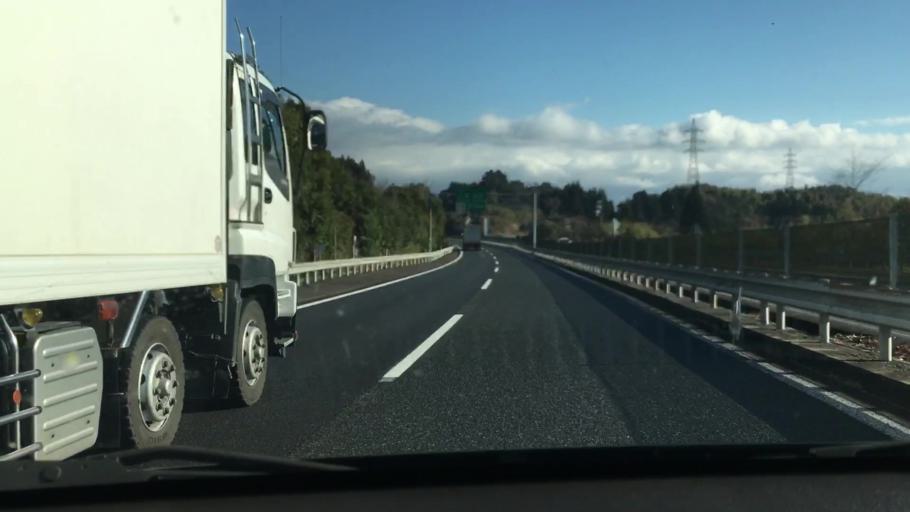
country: JP
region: Kumamoto
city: Hitoyoshi
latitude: 32.2361
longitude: 130.7637
